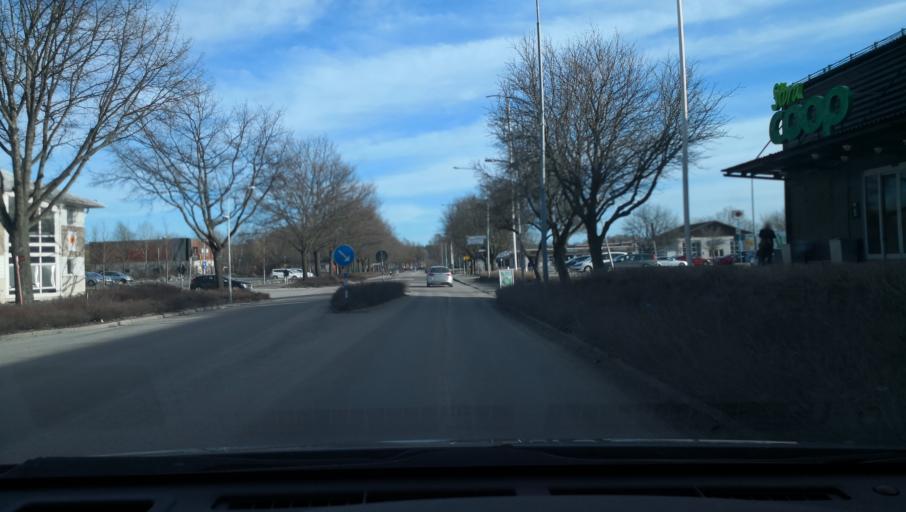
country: SE
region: Uppsala
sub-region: Enkopings Kommun
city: Enkoping
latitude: 59.6335
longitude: 17.0828
